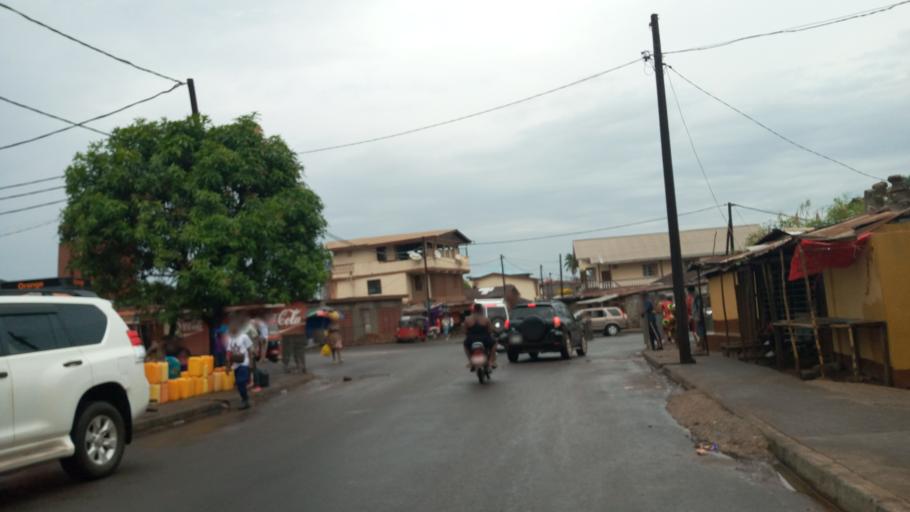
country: SL
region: Western Area
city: Freetown
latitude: 8.4736
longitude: -13.2403
